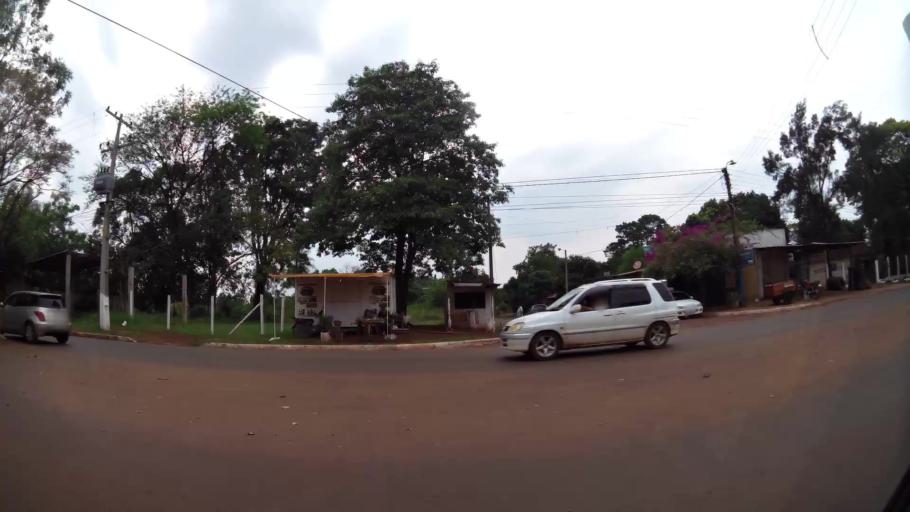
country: PY
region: Alto Parana
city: Presidente Franco
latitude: -25.5271
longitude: -54.6469
